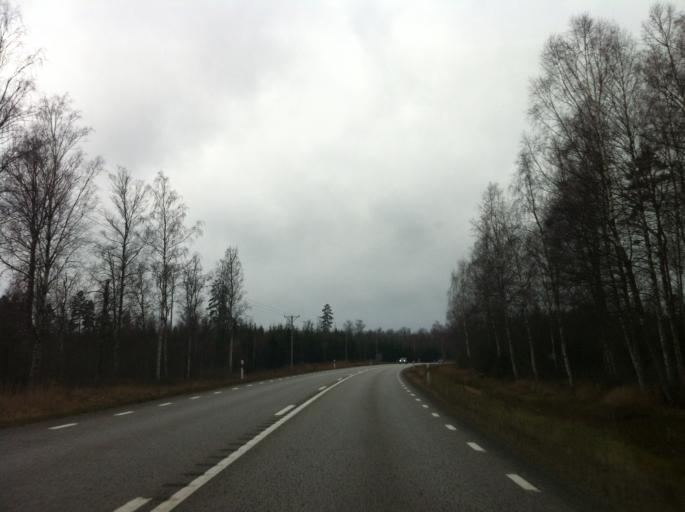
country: SE
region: Joenkoeping
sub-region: Vetlanda Kommun
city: Vetlanda
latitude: 57.4213
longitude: 15.0439
